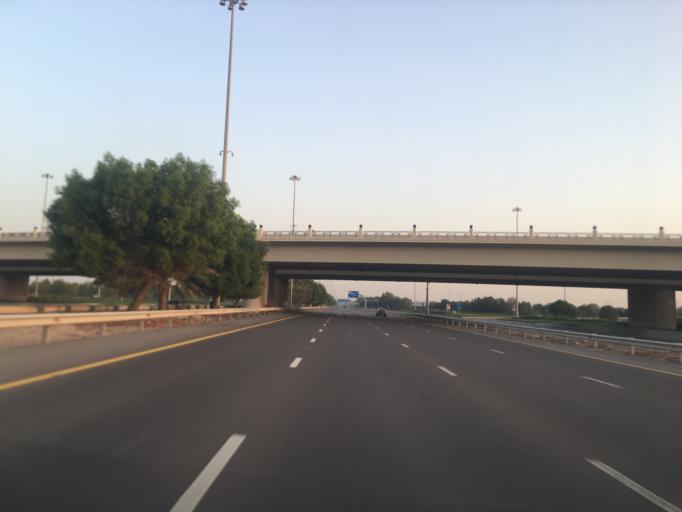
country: AE
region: Abu Dhabi
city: Abu Dhabi
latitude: 24.3749
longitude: 54.5527
